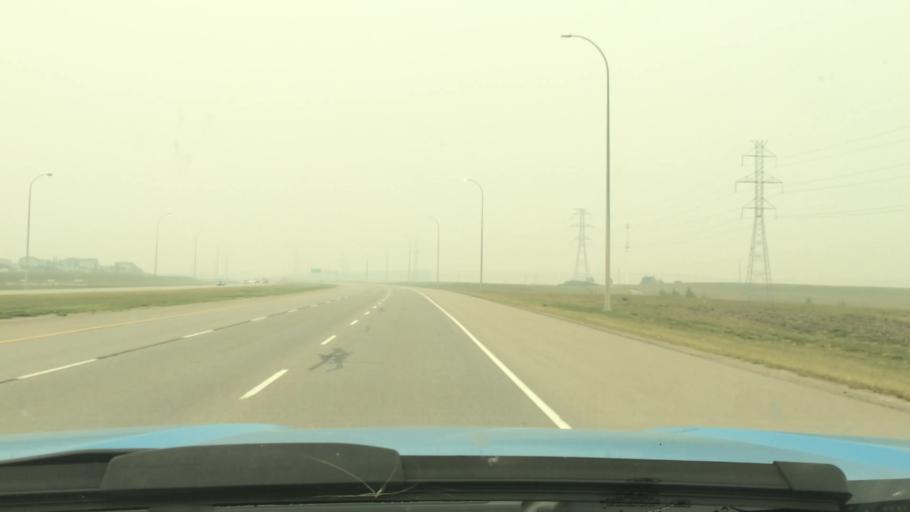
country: CA
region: Alberta
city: Airdrie
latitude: 51.1760
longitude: -114.0392
